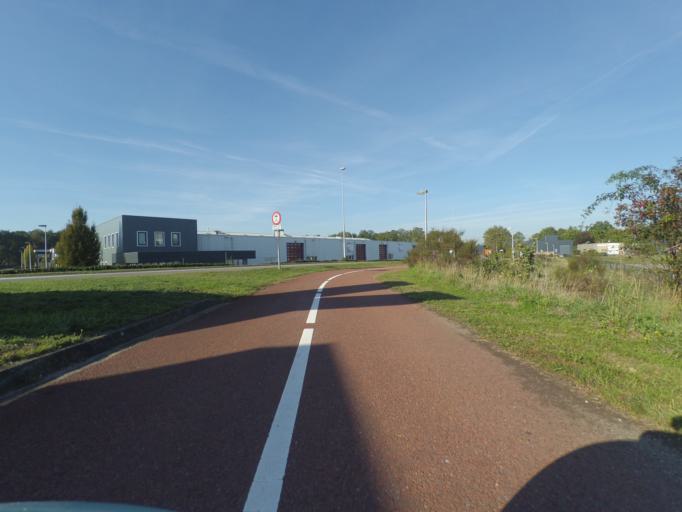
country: NL
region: Gelderland
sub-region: Berkelland
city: Eibergen
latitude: 52.0874
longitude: 6.6425
